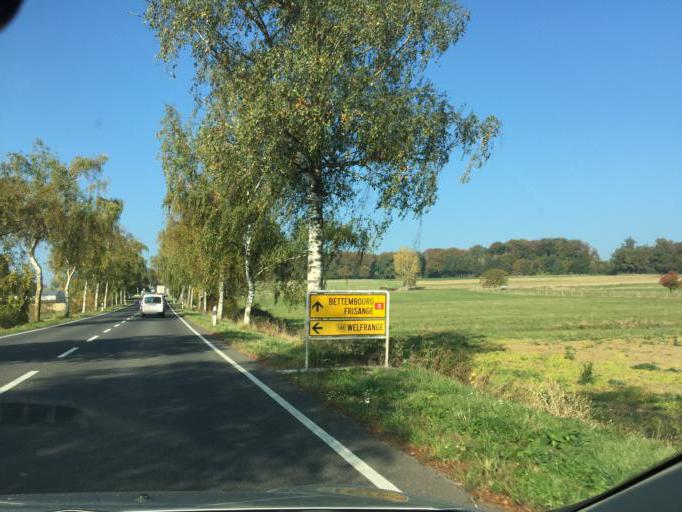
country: LU
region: Grevenmacher
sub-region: Canton de Remich
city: Waldbredimus
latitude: 49.5411
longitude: 6.2908
